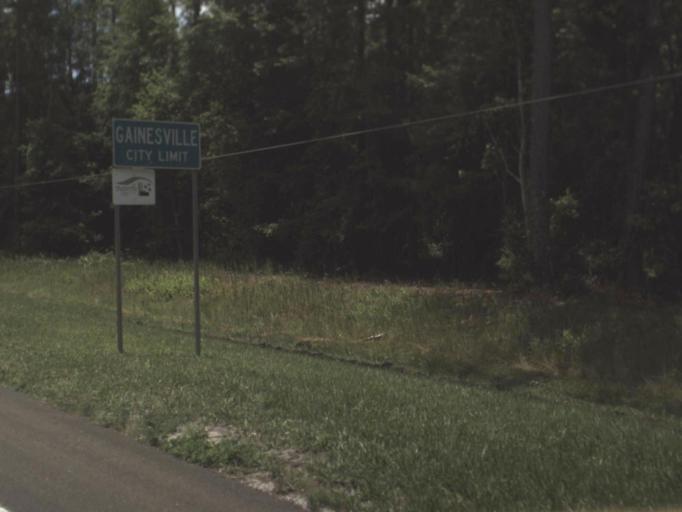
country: US
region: Florida
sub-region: Alachua County
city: Alachua
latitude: 29.7706
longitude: -82.3677
